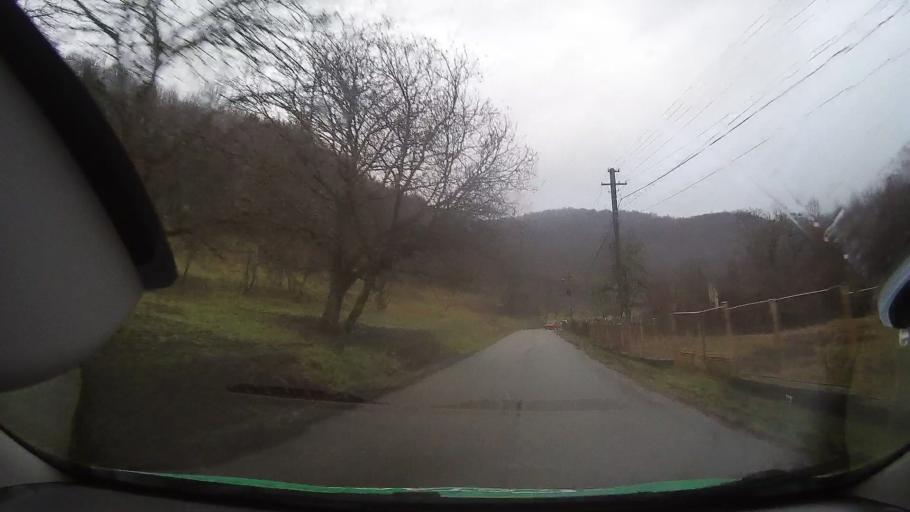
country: RO
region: Alba
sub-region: Comuna Avram Iancu
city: Avram Iancu
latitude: 46.3020
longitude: 22.7608
